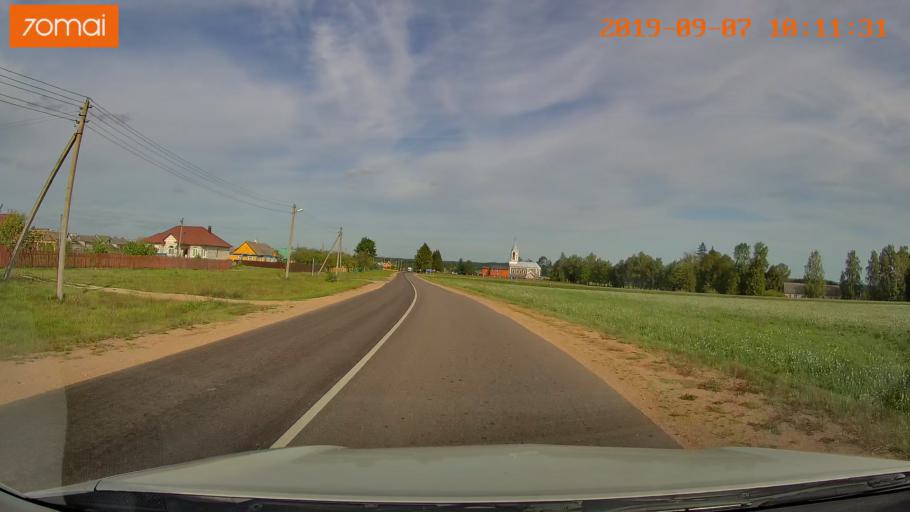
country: BY
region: Grodnenskaya
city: Voranava
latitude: 54.1239
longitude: 25.3656
